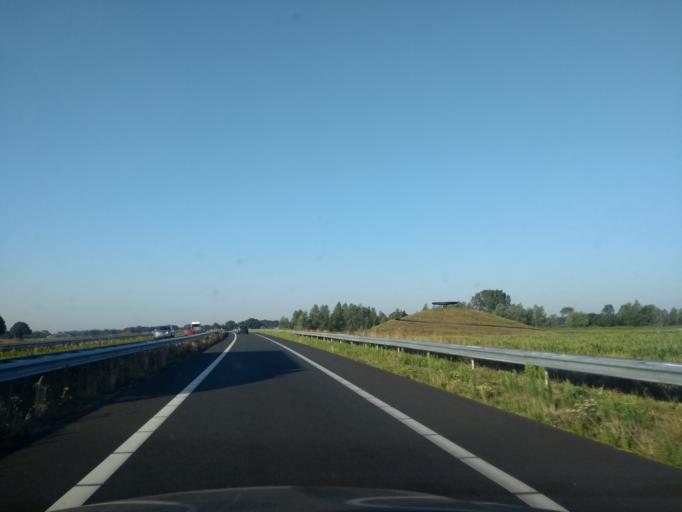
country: NL
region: Gelderland
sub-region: Berkelland
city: Neede
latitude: 52.1127
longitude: 6.6248
